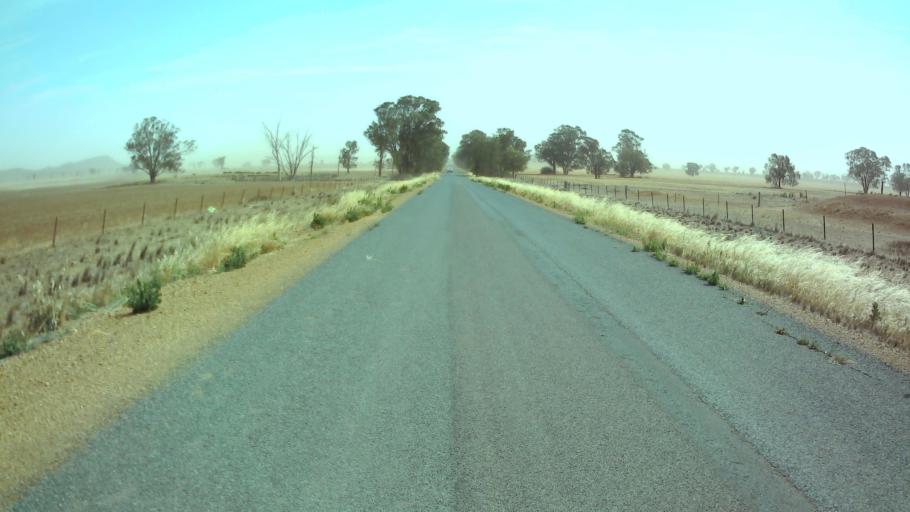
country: AU
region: New South Wales
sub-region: Weddin
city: Grenfell
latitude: -33.7635
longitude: 147.9882
